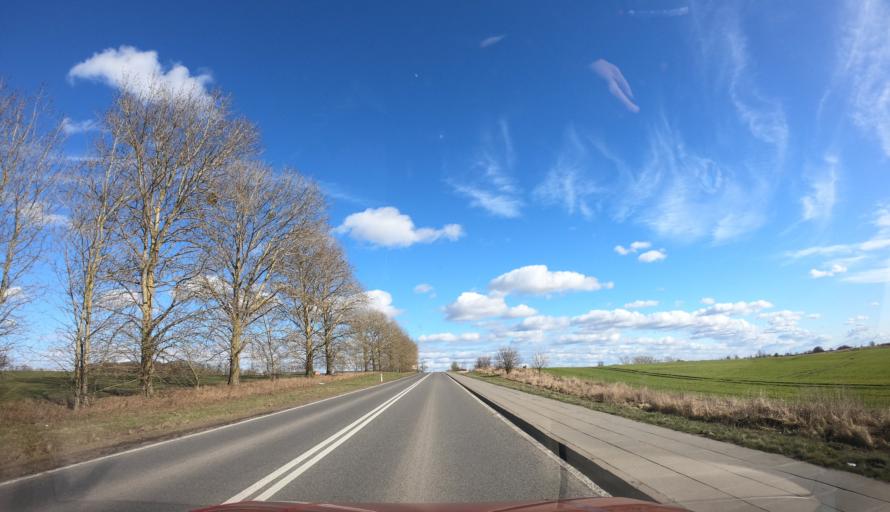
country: PL
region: West Pomeranian Voivodeship
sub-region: Powiat policki
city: Dobra
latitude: 53.4367
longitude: 14.4197
